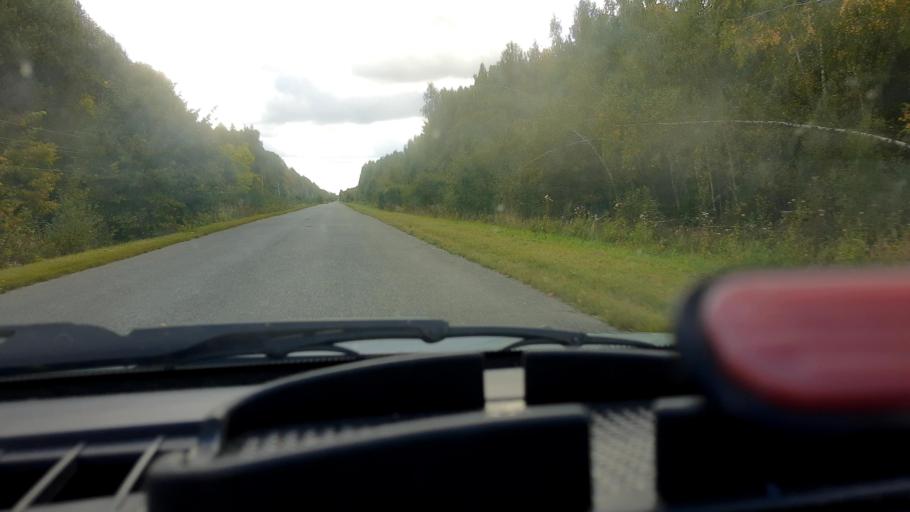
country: RU
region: Mariy-El
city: Kilemary
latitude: 56.9170
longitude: 46.7209
